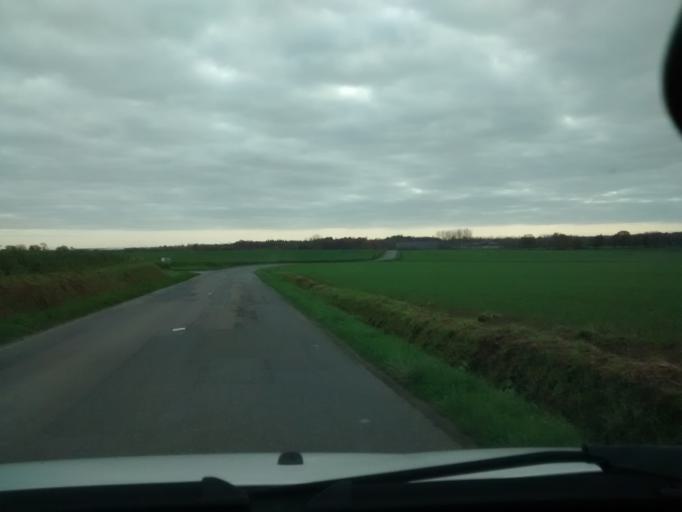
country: FR
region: Brittany
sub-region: Departement d'Ille-et-Vilaine
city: Chavagne
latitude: 48.0779
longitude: -1.7700
